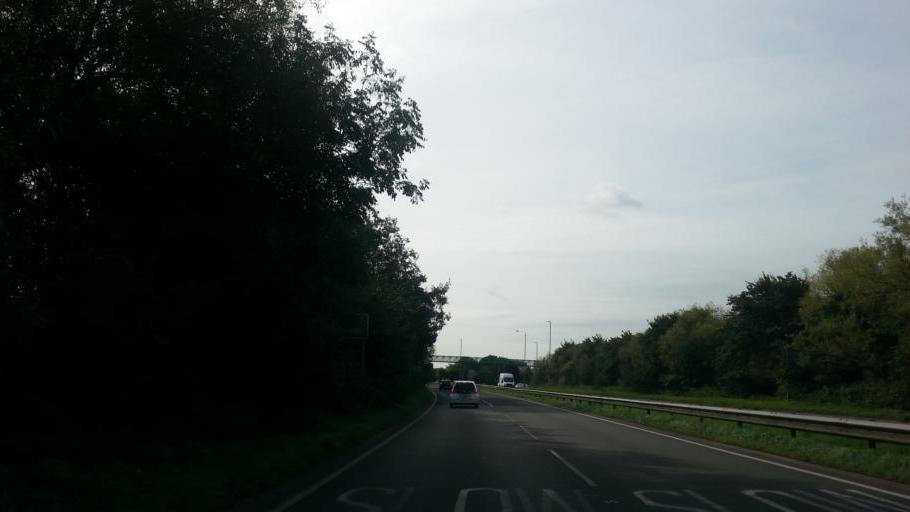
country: GB
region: England
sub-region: Leicestershire
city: Syston
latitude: 52.6870
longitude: -1.0960
